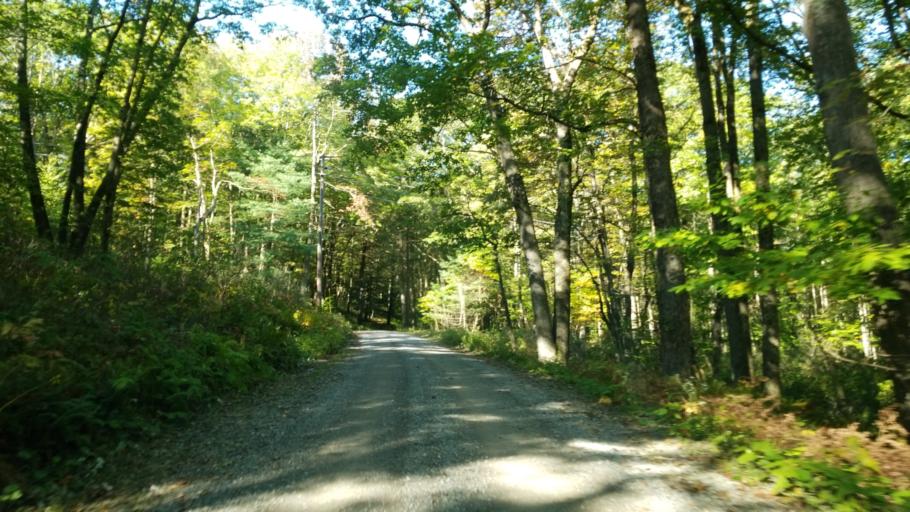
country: US
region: Pennsylvania
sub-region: Clearfield County
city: Curwensville
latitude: 41.0888
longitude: -78.5384
